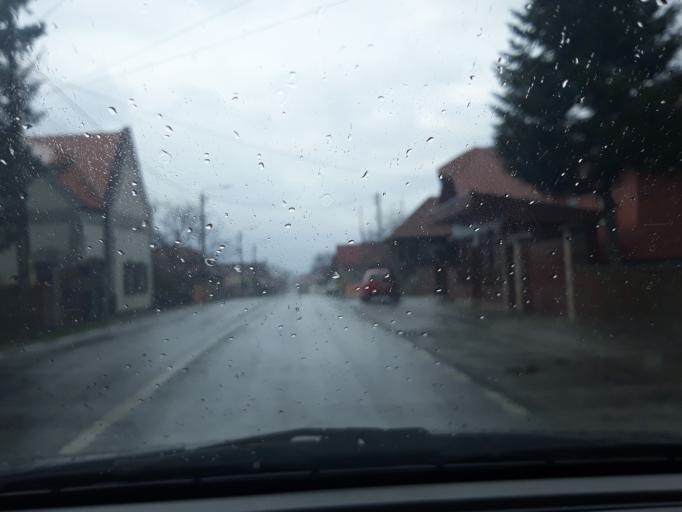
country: RO
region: Harghita
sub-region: Comuna Corund
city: Corund
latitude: 46.4744
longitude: 25.1780
